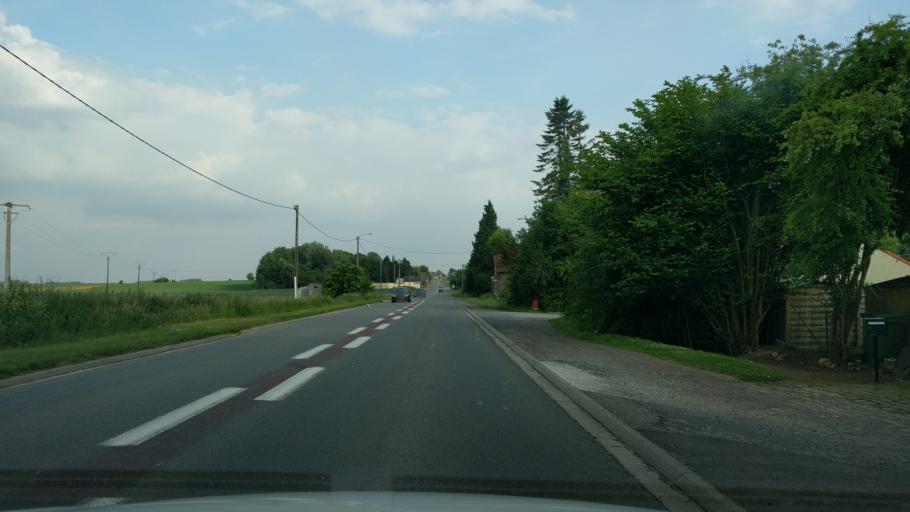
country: FR
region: Nord-Pas-de-Calais
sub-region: Departement du Pas-de-Calais
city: Bapaume
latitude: 50.0666
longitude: 2.8900
